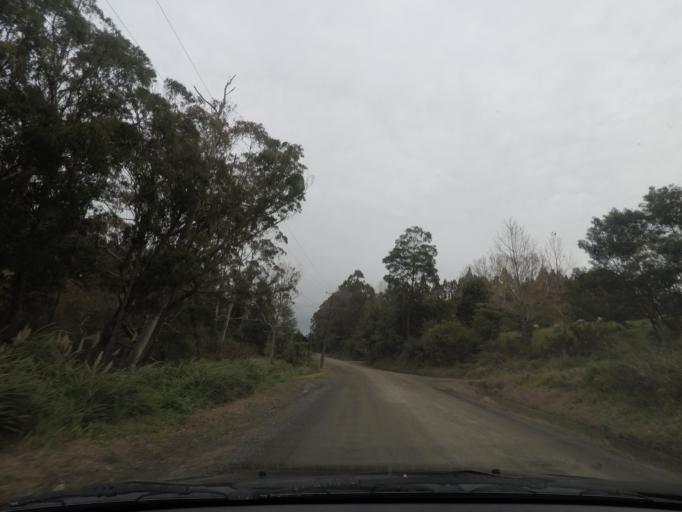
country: NZ
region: Auckland
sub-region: Auckland
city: Muriwai Beach
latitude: -36.7535
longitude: 174.5753
